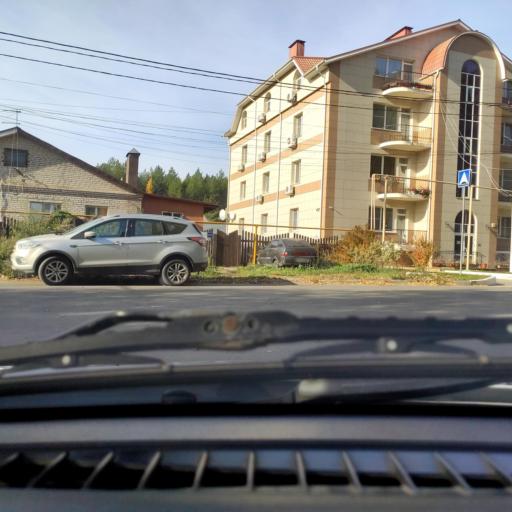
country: RU
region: Samara
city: Tol'yatti
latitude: 53.5293
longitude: 49.3907
